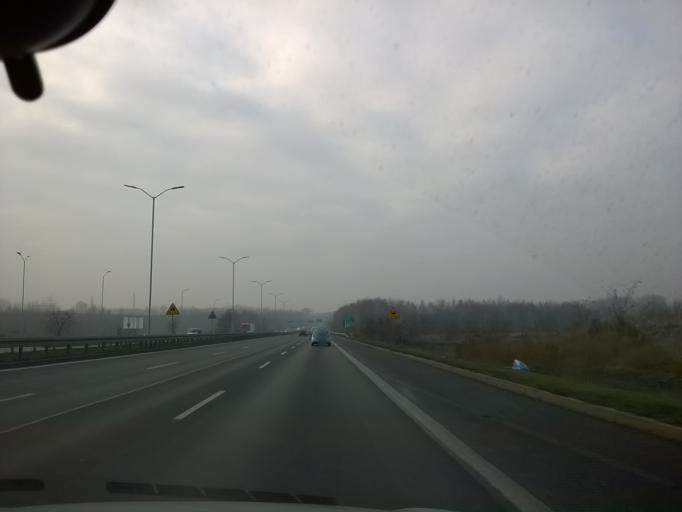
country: PL
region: Silesian Voivodeship
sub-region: Swietochlowice
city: Swietochlowice
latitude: 50.2961
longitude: 18.8960
